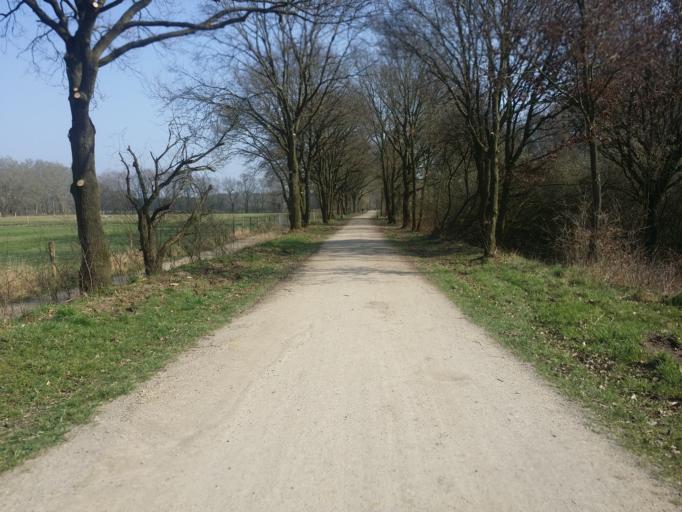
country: DE
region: Lower Saxony
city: Delmenhorst
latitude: 53.0149
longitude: 8.6647
